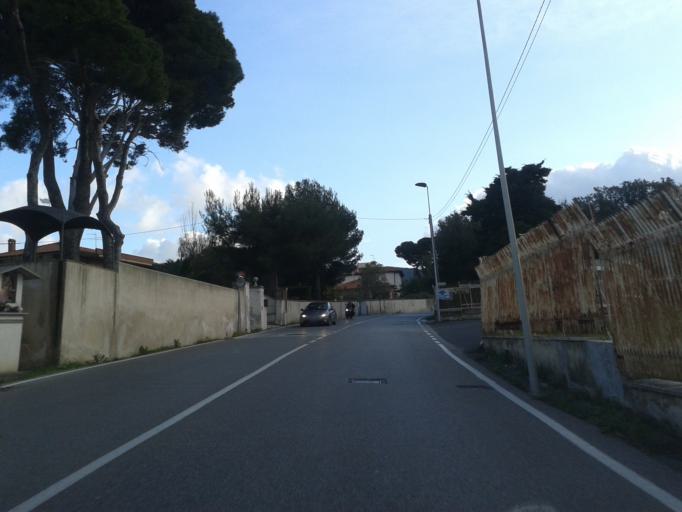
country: IT
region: Tuscany
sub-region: Provincia di Livorno
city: Livorno
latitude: 43.5082
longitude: 10.3359
